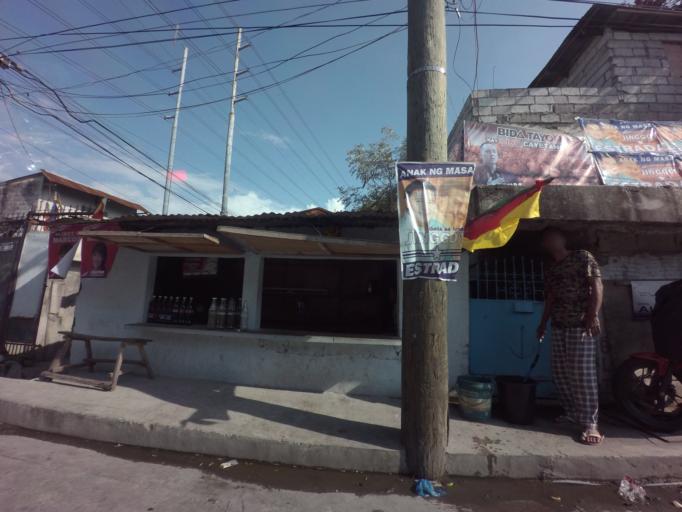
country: PH
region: Calabarzon
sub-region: Province of Rizal
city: Taguig
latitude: 14.4991
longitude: 121.0590
